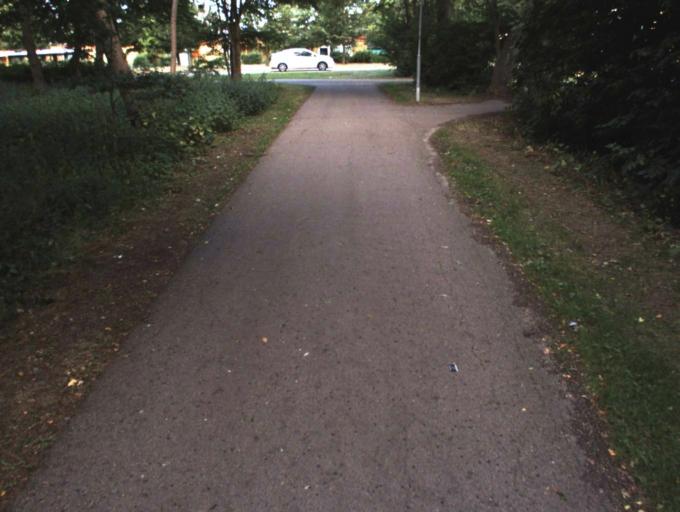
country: SE
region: Skane
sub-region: Helsingborg
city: Helsingborg
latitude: 56.0458
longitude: 12.7472
